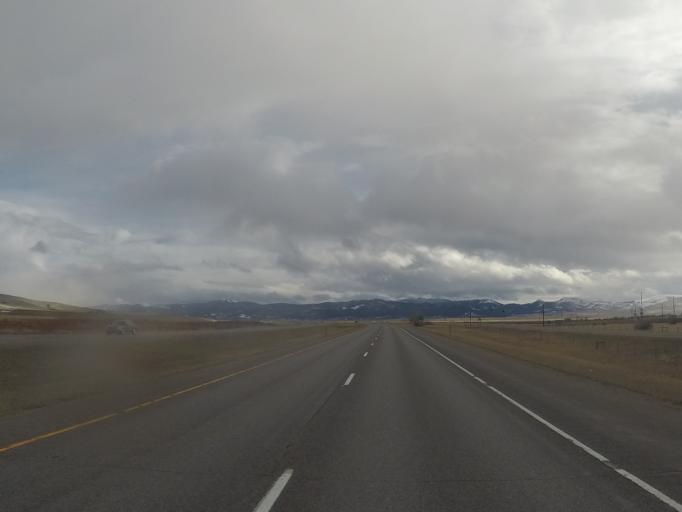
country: US
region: Montana
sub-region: Deer Lodge County
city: Warm Springs
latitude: 46.1719
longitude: -112.7874
